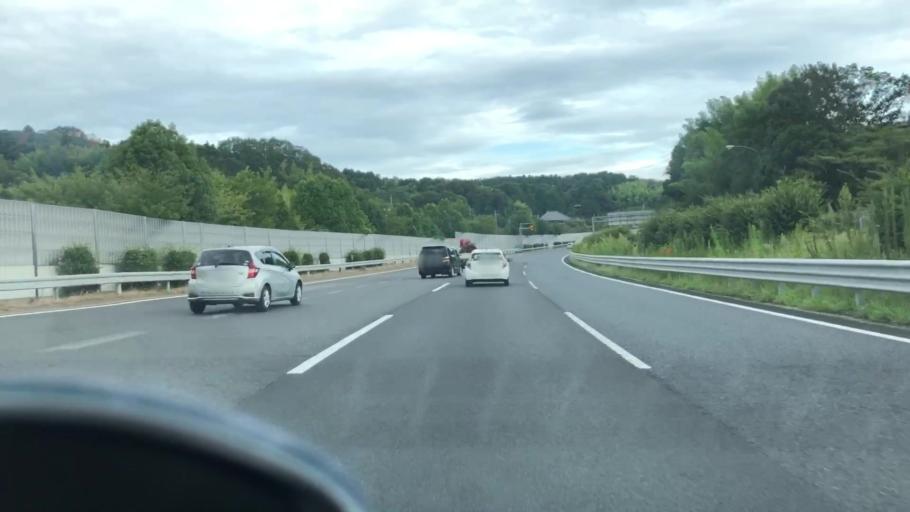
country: JP
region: Hyogo
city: Sandacho
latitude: 34.8930
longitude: 135.1551
